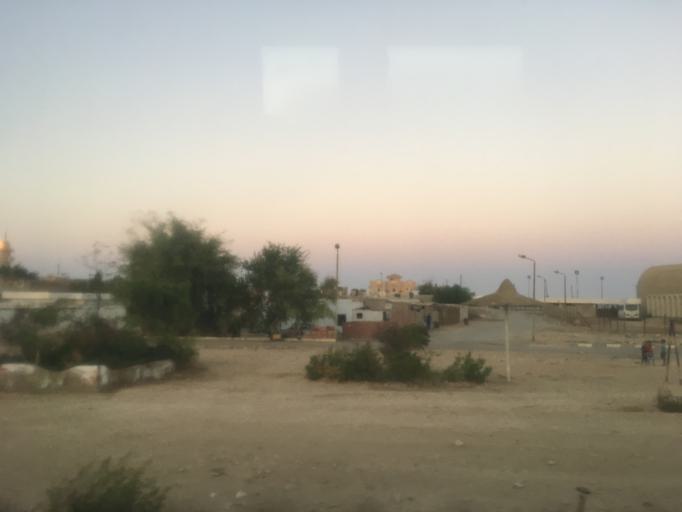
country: EG
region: Red Sea
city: Al Qusayr
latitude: 26.2658
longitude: 34.1949
